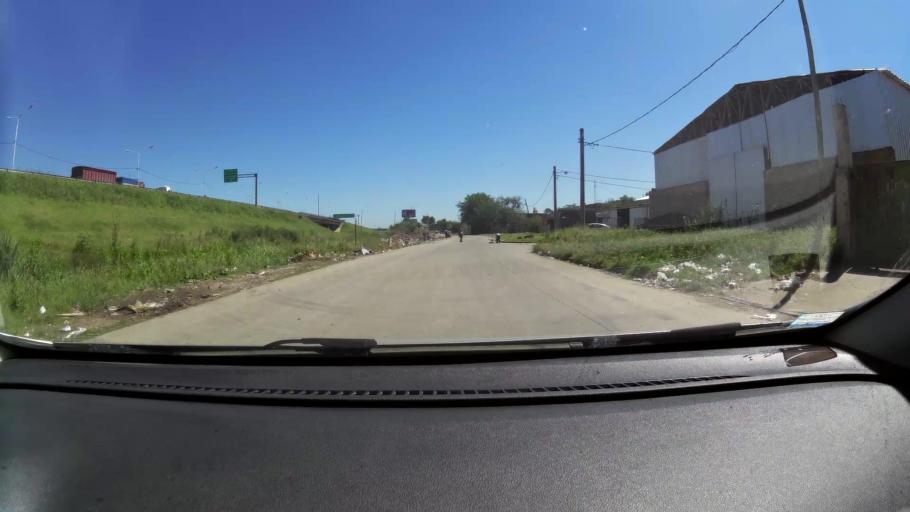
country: AR
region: Santa Fe
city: Perez
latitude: -32.9550
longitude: -60.7211
